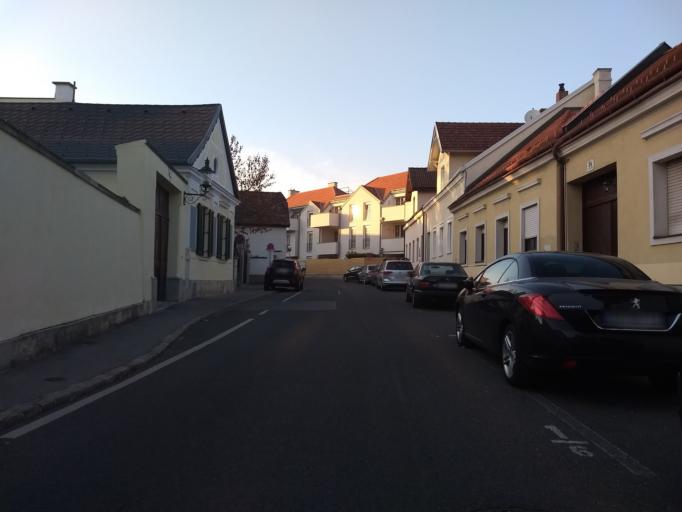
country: AT
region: Lower Austria
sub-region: Politischer Bezirk Modling
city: Perchtoldsdorf
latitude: 48.1279
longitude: 16.2607
